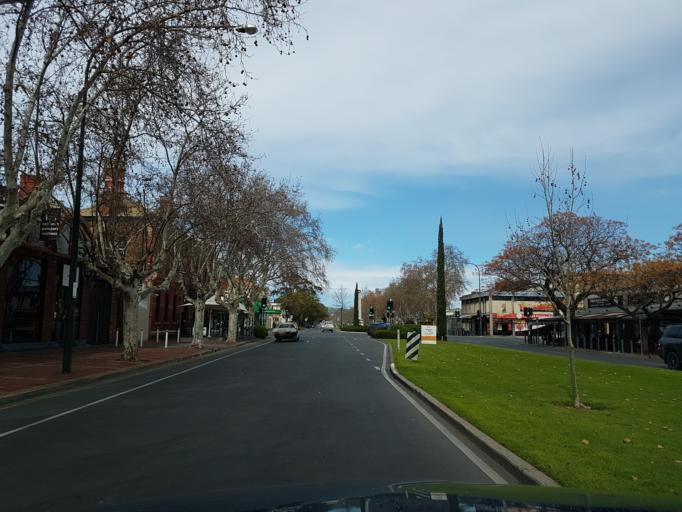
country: AU
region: South Australia
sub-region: Norwood Payneham St Peters
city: Trinity Gardens
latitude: -34.9207
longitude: 138.6320
